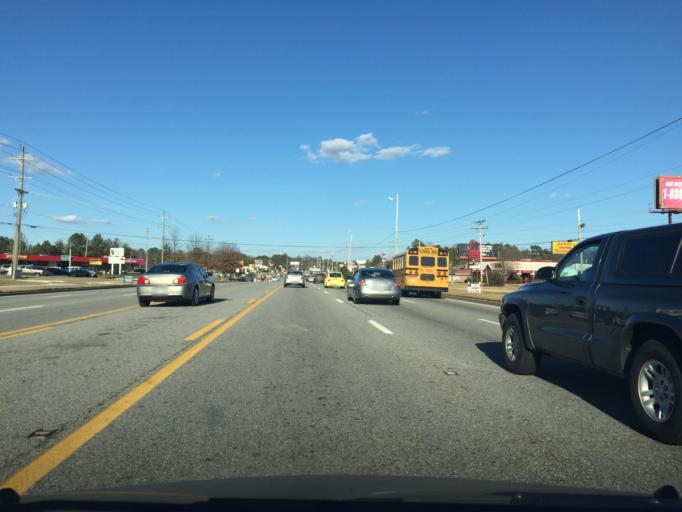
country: US
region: Tennessee
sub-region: Hamilton County
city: Harrison
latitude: 35.0879
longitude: -85.1891
